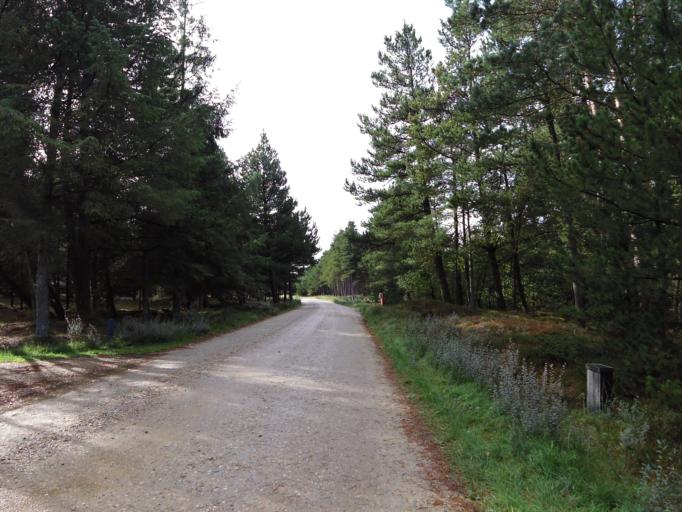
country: DK
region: South Denmark
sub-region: Varde Kommune
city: Oksbol
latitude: 55.5524
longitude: 8.2115
